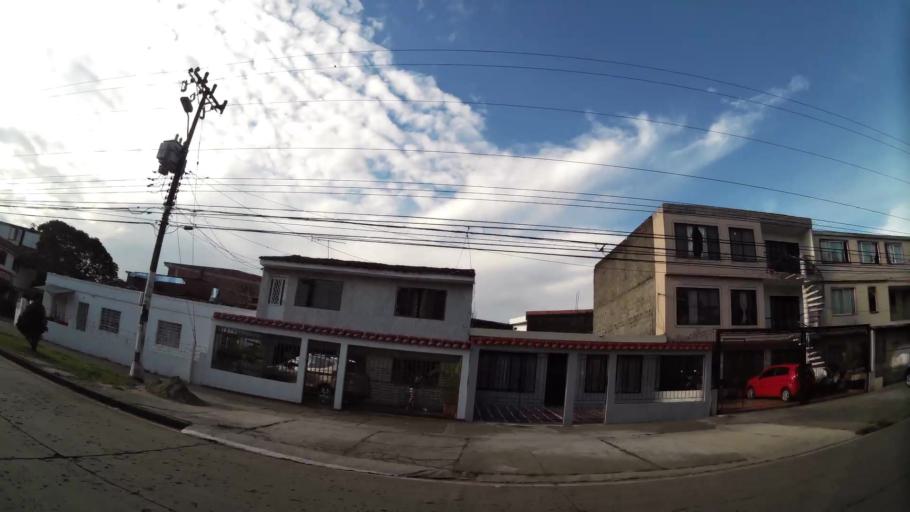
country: CO
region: Valle del Cauca
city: Cali
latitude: 3.4323
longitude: -76.5227
